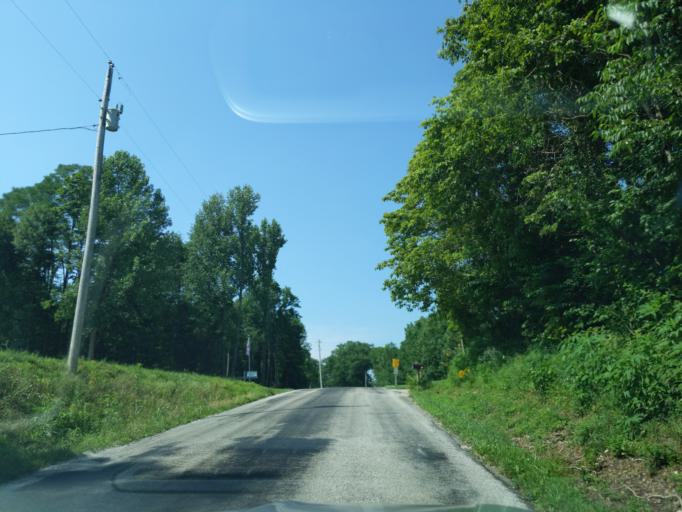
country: US
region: Indiana
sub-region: Ripley County
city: Osgood
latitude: 39.1085
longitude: -85.3440
